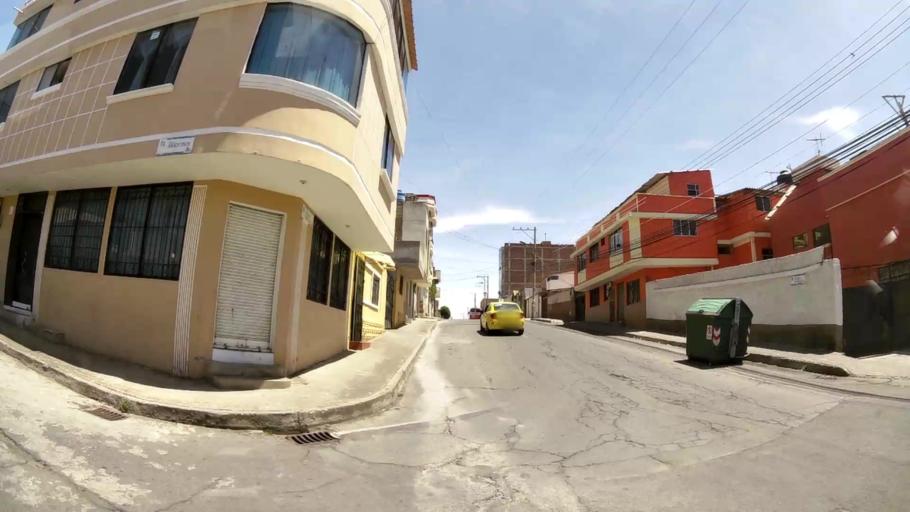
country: EC
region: Chimborazo
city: Riobamba
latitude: -1.6604
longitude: -78.6596
